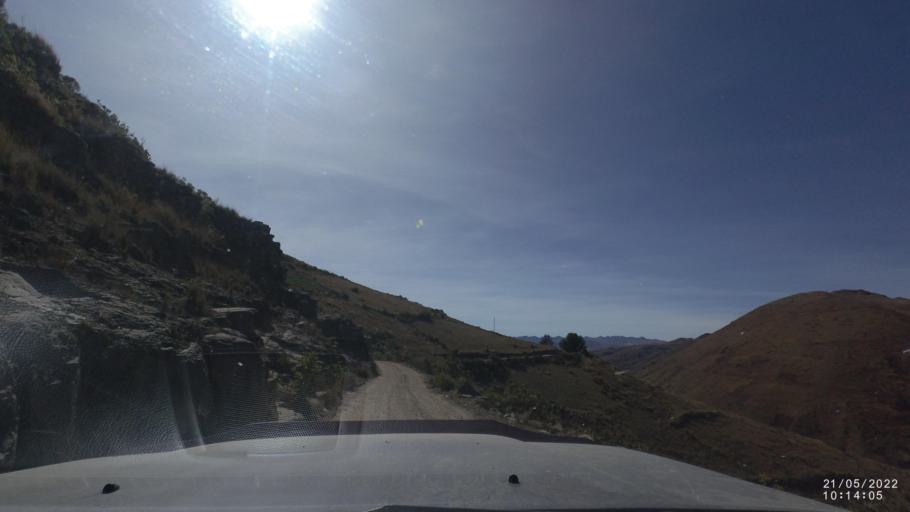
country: BO
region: Cochabamba
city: Colomi
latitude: -17.3331
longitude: -65.9726
